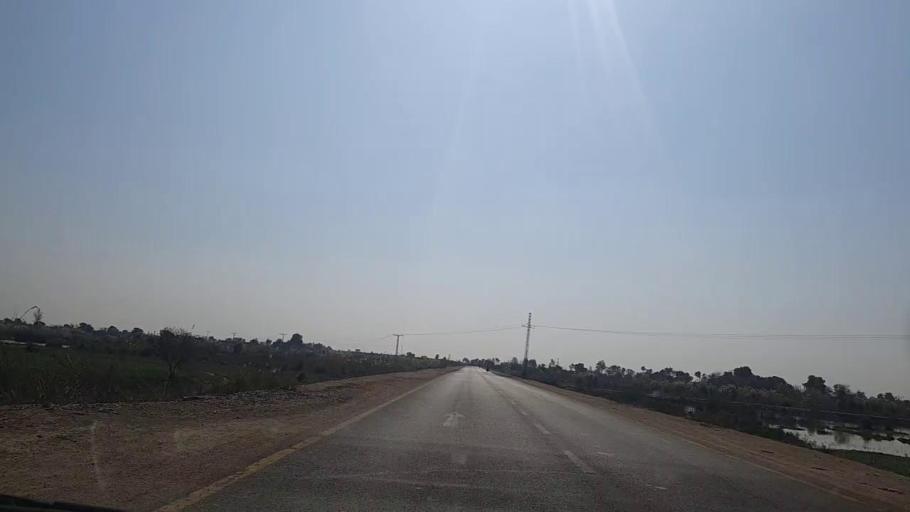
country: PK
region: Sindh
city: Sakrand
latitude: 26.0999
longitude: 68.4034
